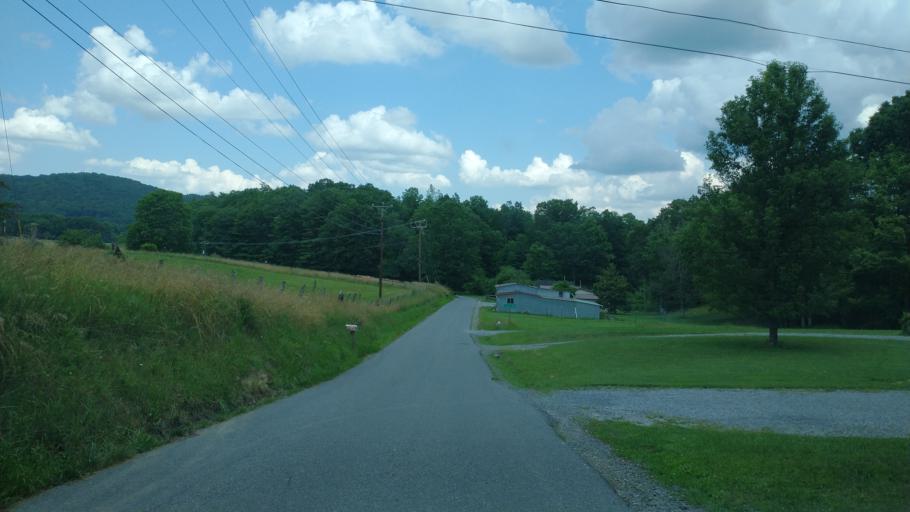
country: US
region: West Virginia
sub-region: Mercer County
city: Athens
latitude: 37.4584
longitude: -81.0226
